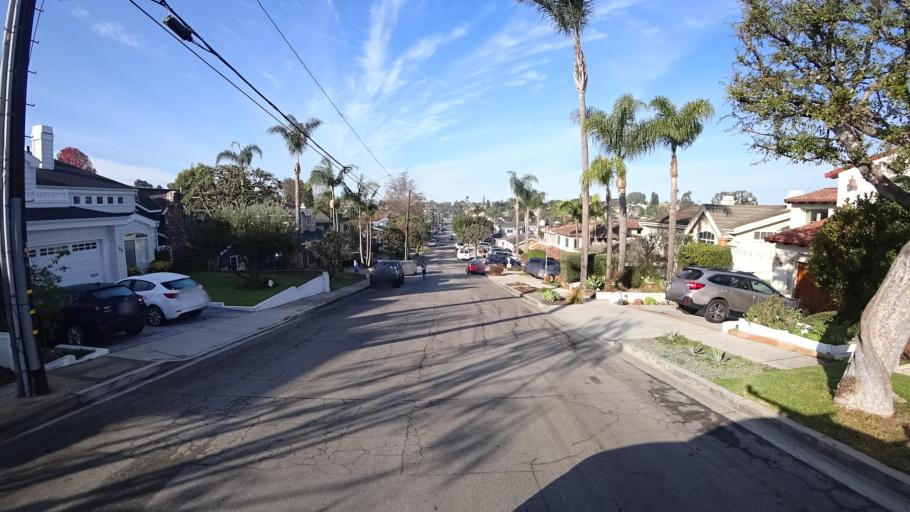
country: US
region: California
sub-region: Los Angeles County
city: Manhattan Beach
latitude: 33.8837
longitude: -118.3902
